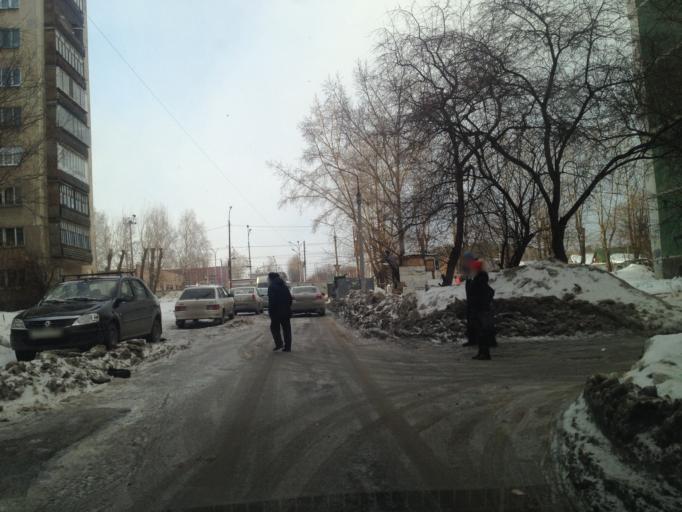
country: RU
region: Sverdlovsk
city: Yekaterinburg
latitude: 56.9102
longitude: 60.5960
